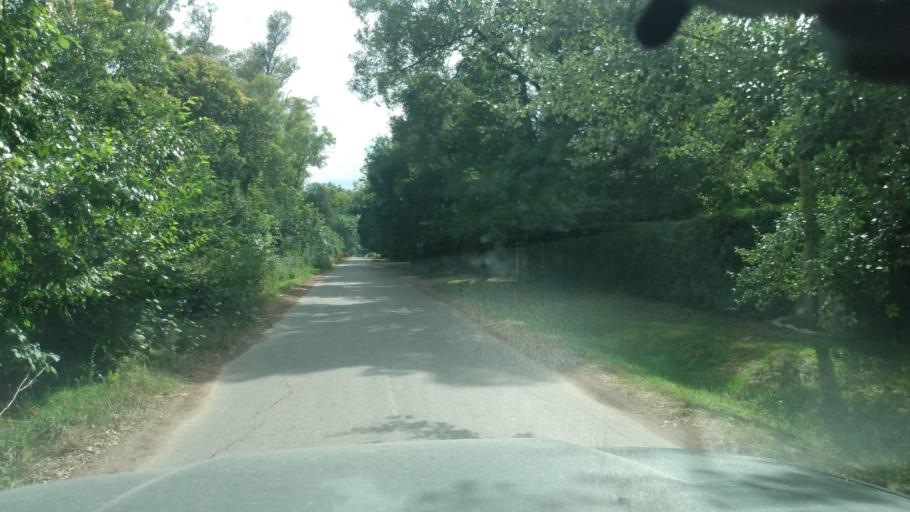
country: AR
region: Buenos Aires
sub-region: Partido de Lujan
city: Lujan
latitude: -34.5913
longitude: -59.0555
